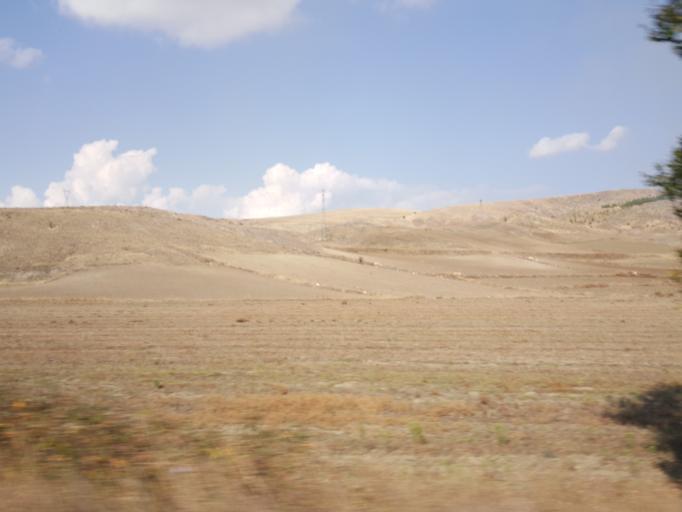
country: TR
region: Corum
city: Bogazkale
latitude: 40.1570
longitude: 34.6092
